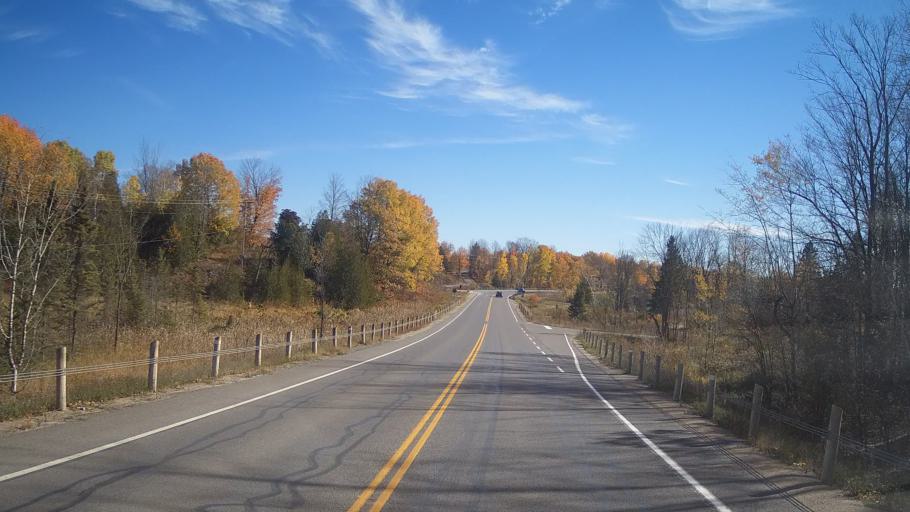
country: CA
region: Ontario
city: Perth
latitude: 44.7352
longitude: -76.6820
